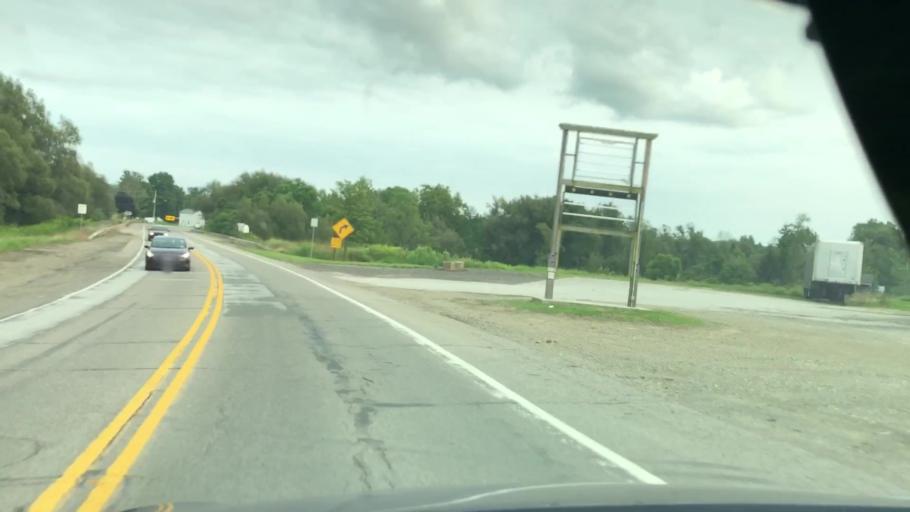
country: US
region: Pennsylvania
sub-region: Erie County
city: Union City
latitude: 42.0066
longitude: -79.8137
